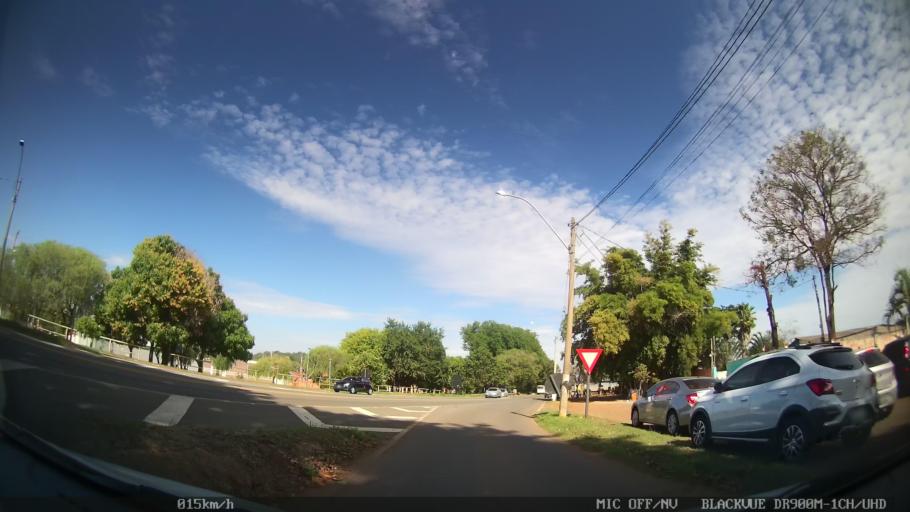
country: BR
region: Sao Paulo
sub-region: Santa Barbara D'Oeste
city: Santa Barbara d'Oeste
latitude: -22.7465
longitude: -47.4272
